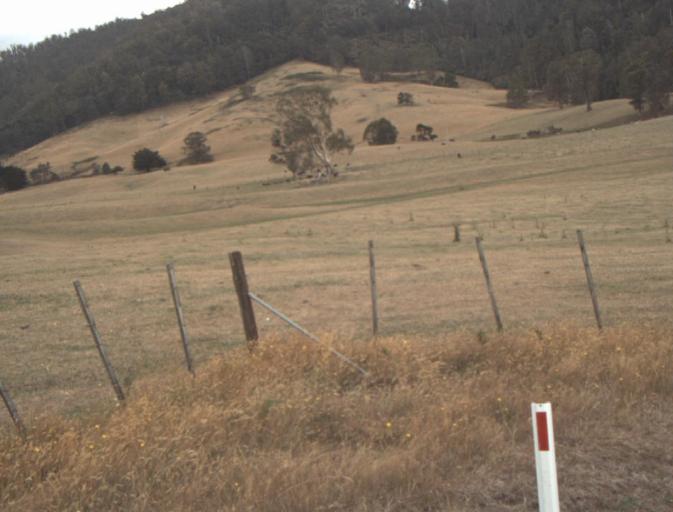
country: AU
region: Tasmania
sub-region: Dorset
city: Scottsdale
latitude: -41.4550
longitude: 147.5994
